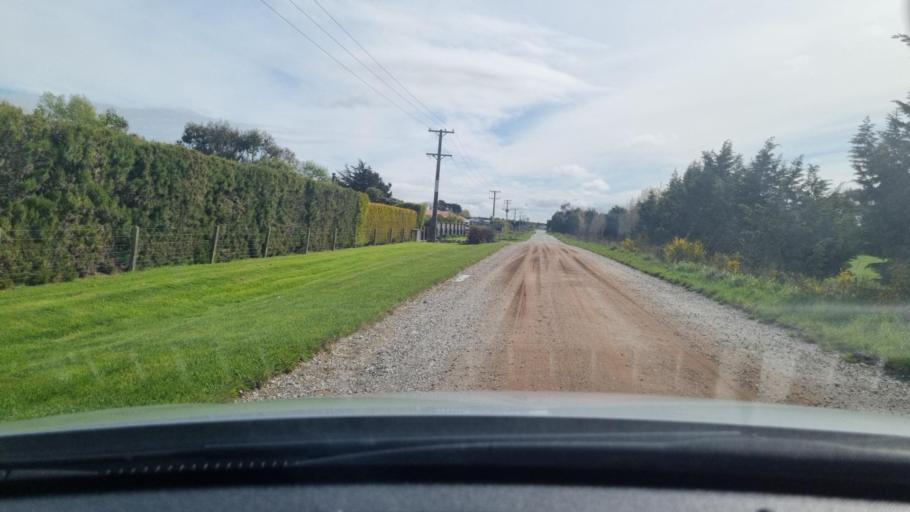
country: NZ
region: Southland
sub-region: Invercargill City
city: Invercargill
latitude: -46.4507
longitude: 168.3882
